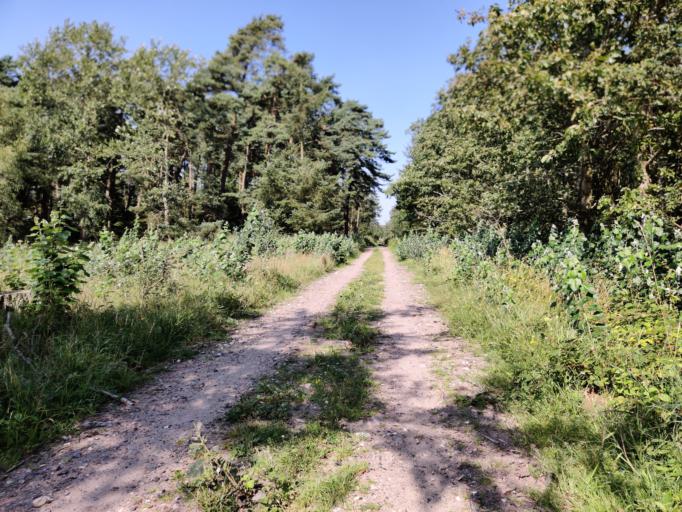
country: DK
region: Zealand
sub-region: Guldborgsund Kommune
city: Nykobing Falster
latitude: 54.6204
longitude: 11.9565
